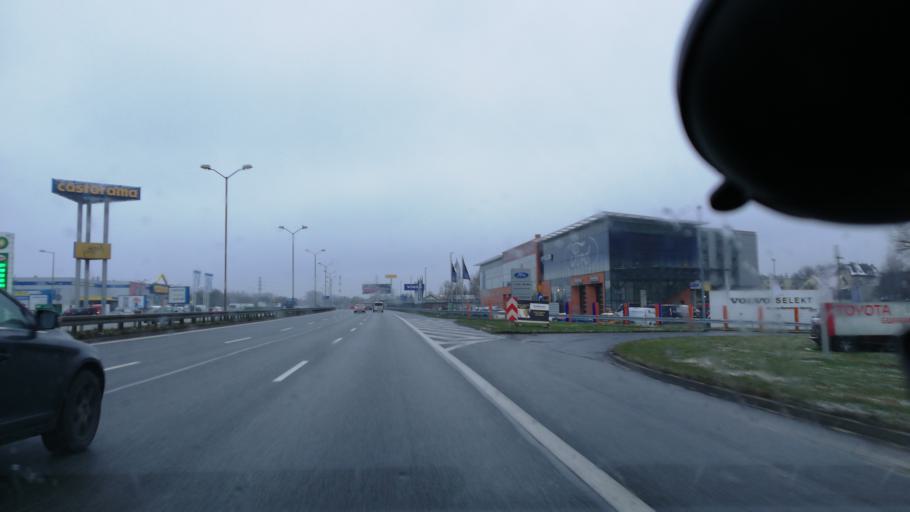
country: PL
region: Silesian Voivodeship
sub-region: Chorzow
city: Chorzow
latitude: 50.2795
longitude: 18.9536
